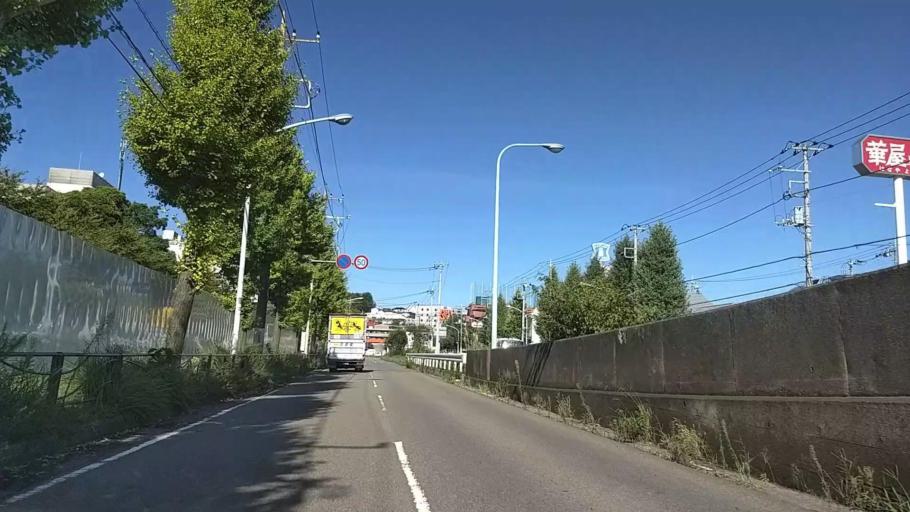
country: JP
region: Tokyo
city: Chofugaoka
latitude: 35.5819
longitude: 139.6070
